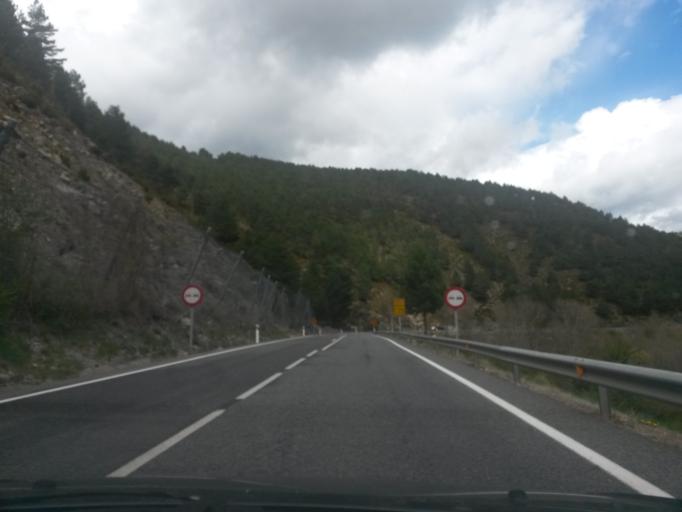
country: ES
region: Catalonia
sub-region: Provincia de Lleida
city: Lles de Cerdanya
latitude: 42.3627
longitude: 1.7047
